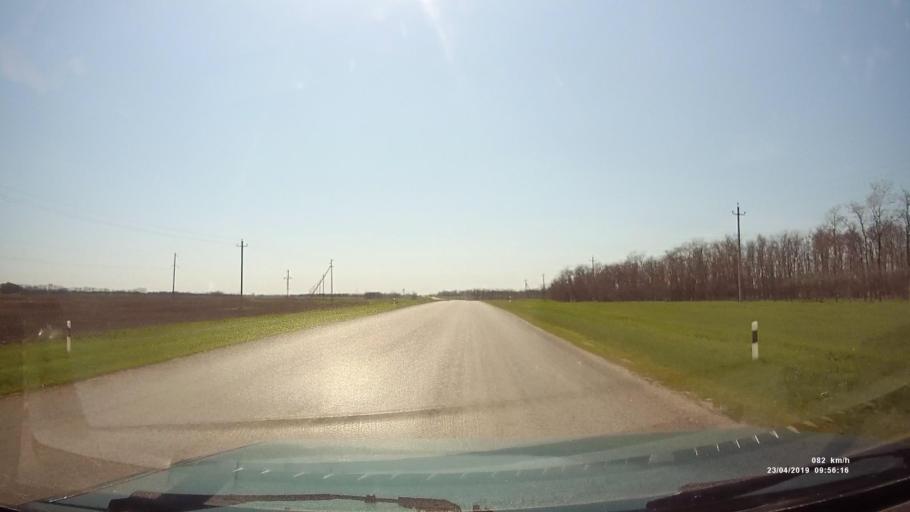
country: RU
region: Rostov
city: Orlovskiy
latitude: 46.7997
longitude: 42.0698
